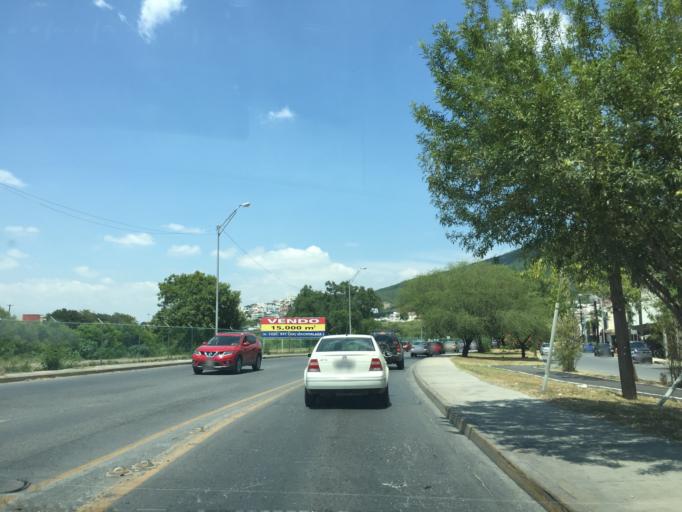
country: MX
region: Nuevo Leon
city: Guadalupe
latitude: 25.6476
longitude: -100.2726
